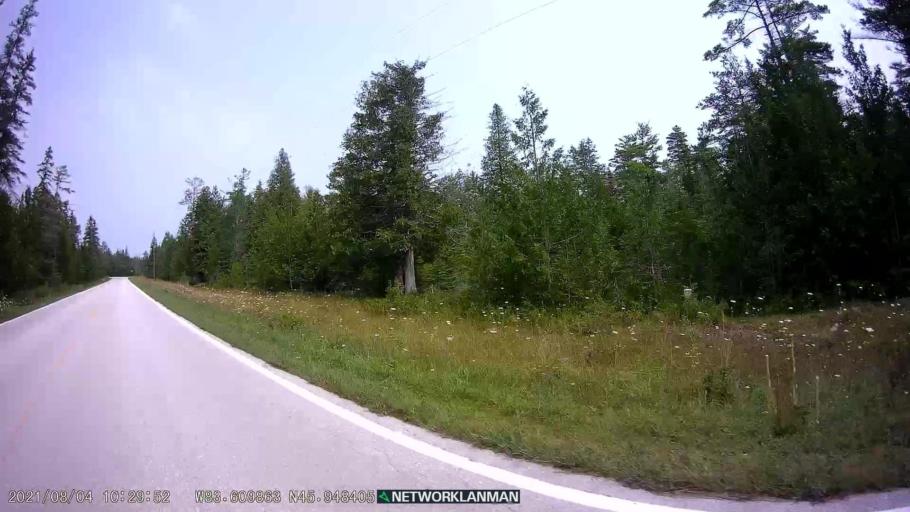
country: CA
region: Ontario
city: Thessalon
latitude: 45.9486
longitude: -83.6099
